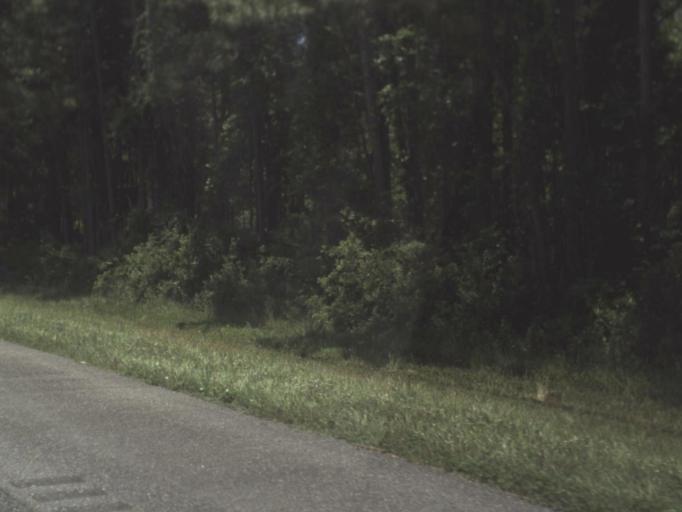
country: US
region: Florida
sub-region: Columbia County
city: Watertown
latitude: 30.2540
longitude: -82.4225
